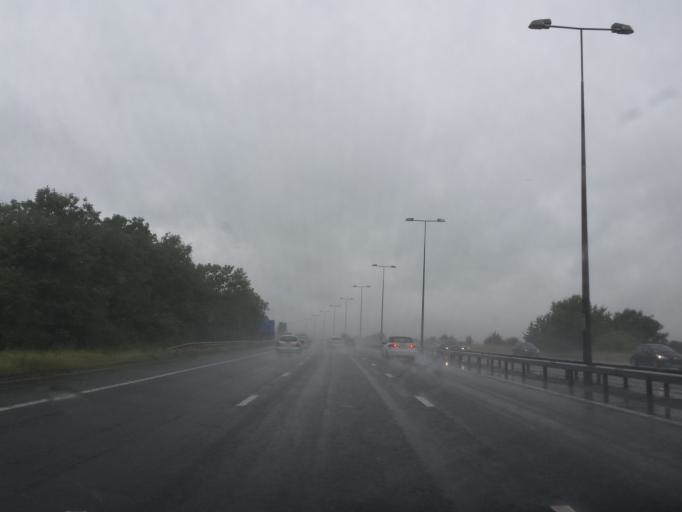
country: GB
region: England
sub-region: Derbyshire
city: Long Eaton
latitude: 52.9078
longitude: -1.3004
